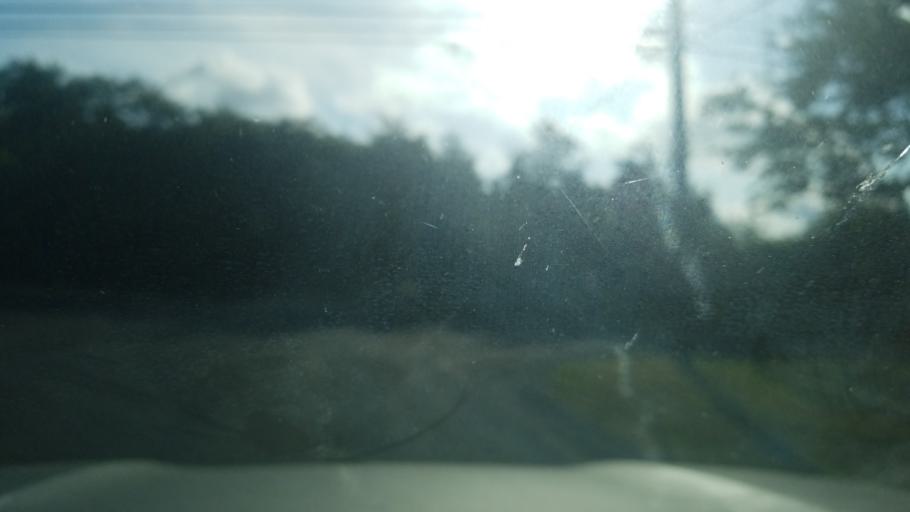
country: US
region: Texas
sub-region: Bexar County
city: Timberwood Park
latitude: 29.6975
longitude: -98.5160
